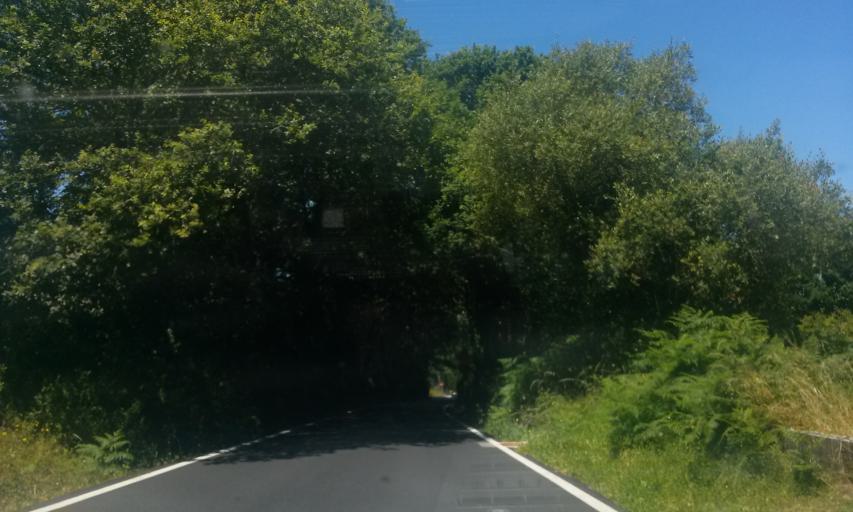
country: ES
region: Galicia
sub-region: Provincia de Lugo
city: Lugo
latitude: 43.0246
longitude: -7.5766
